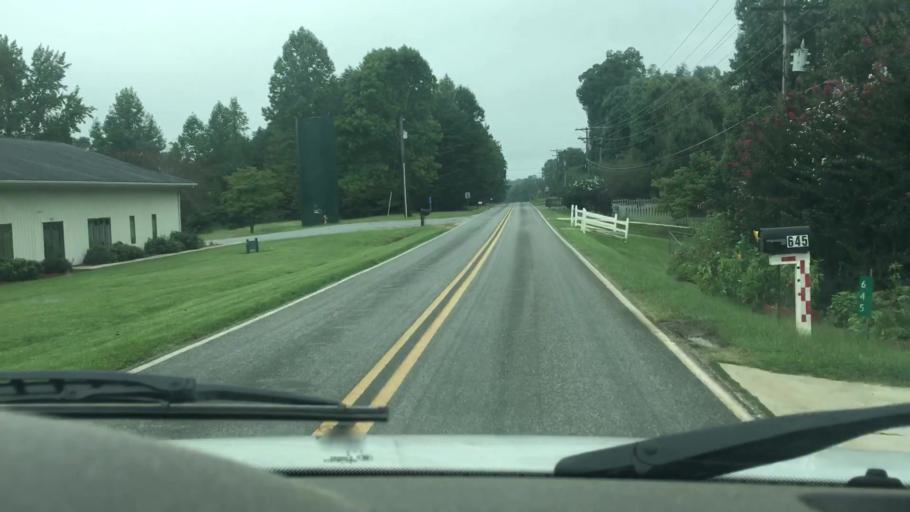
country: US
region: North Carolina
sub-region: Gaston County
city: Davidson
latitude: 35.5203
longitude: -80.8033
